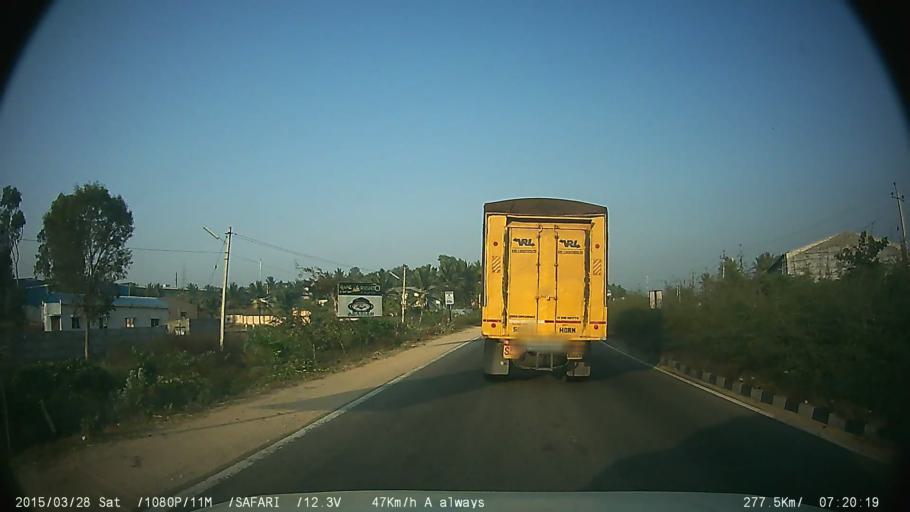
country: IN
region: Karnataka
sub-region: Mandya
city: Mandya
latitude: 12.4974
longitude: 76.8134
